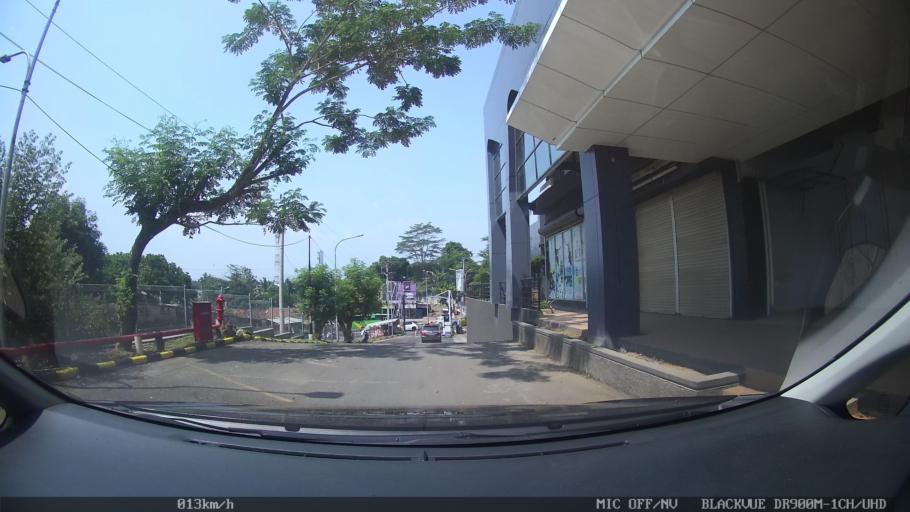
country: ID
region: Lampung
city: Kedaton
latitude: -5.3706
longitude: 105.2375
